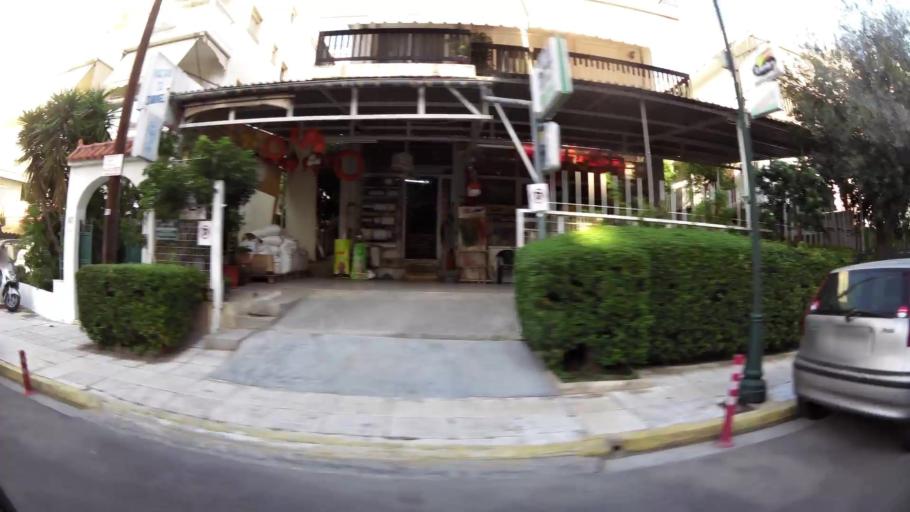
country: GR
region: Attica
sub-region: Nomarchia Athinas
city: Argyroupoli
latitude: 37.8874
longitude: 23.7707
